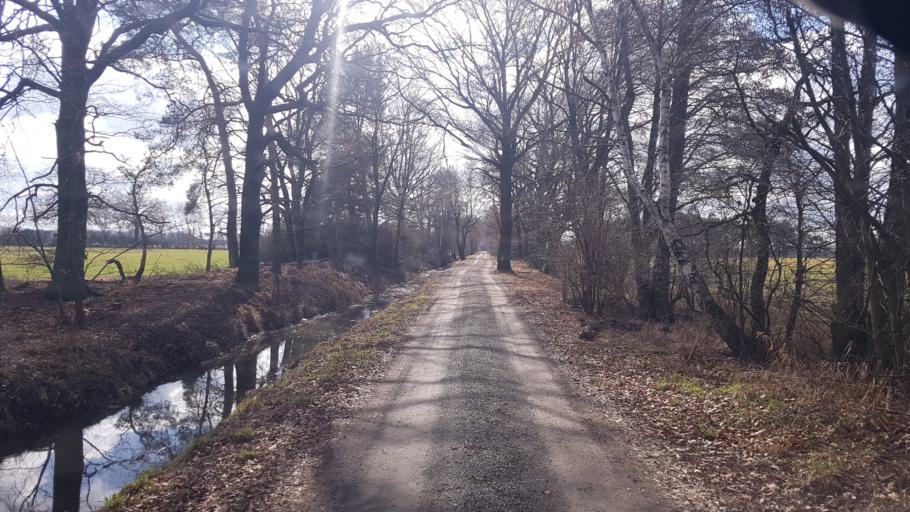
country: DE
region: Brandenburg
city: Falkenberg
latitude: 51.6065
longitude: 13.2192
